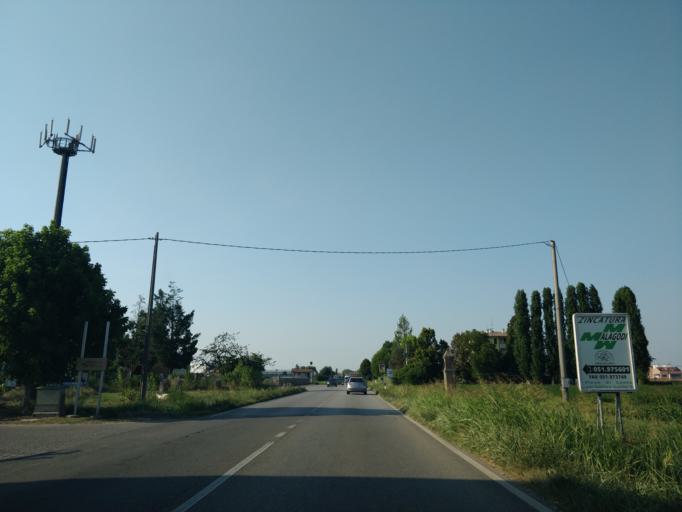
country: IT
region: Emilia-Romagna
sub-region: Provincia di Bologna
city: Pieve di Cento
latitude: 44.7042
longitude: 11.3054
